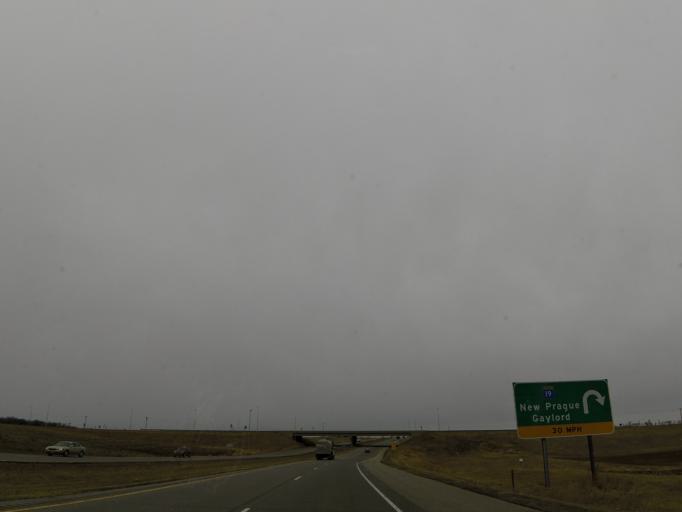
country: US
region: Minnesota
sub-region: Le Sueur County
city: Le Sueur
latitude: 44.5404
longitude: -93.8491
